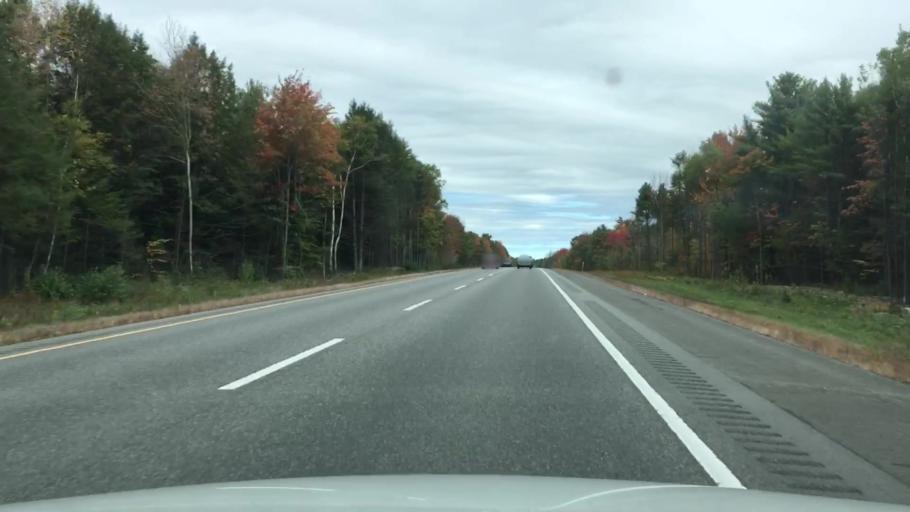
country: US
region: Maine
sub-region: Kennebec County
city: Sidney
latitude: 44.4268
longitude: -69.7371
